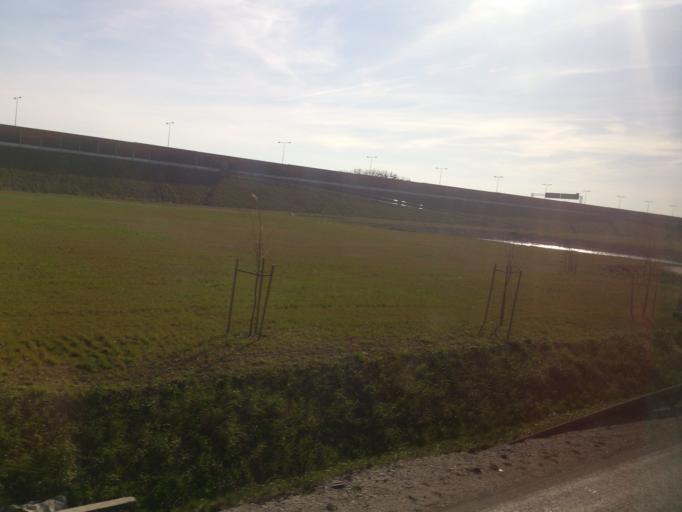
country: PL
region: Kujawsko-Pomorskie
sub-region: Powiat aleksandrowski
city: Ciechocinek
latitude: 52.8698
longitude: 18.7522
